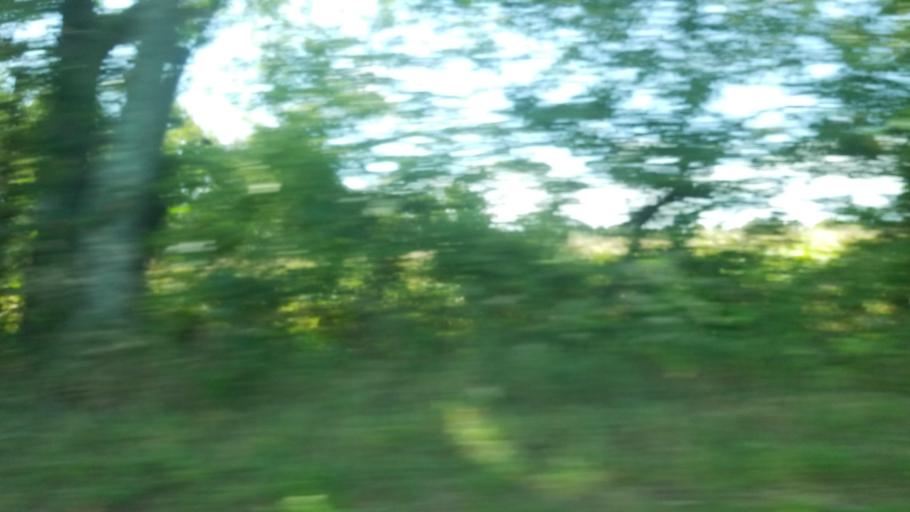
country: US
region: Illinois
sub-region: Williamson County
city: Johnston City
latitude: 37.7868
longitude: -88.8175
